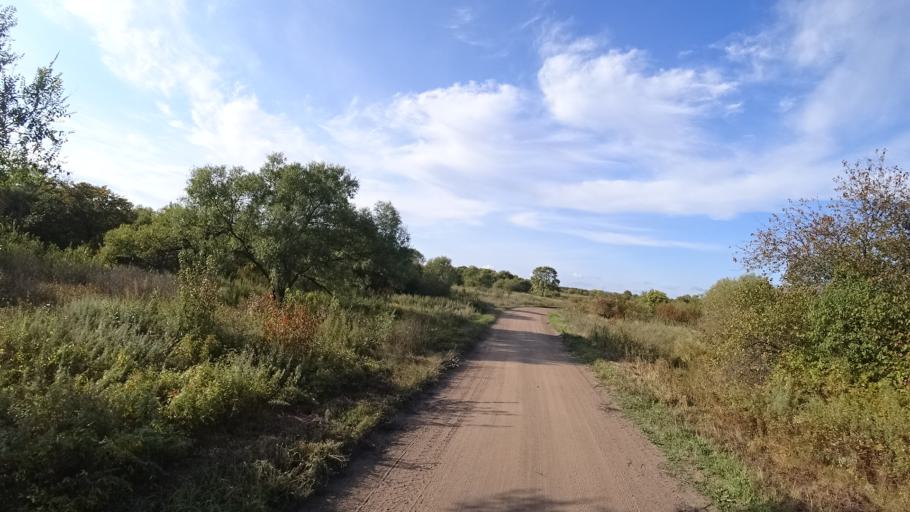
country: RU
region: Amur
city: Arkhara
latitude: 49.3501
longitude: 130.1009
